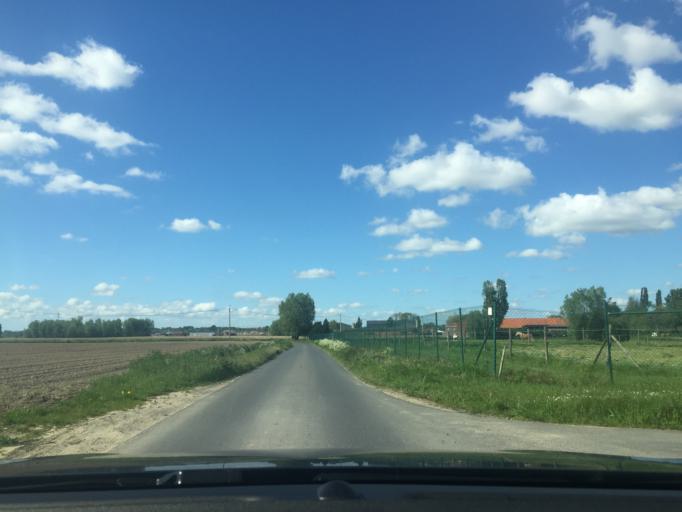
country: BE
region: Flanders
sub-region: Provincie West-Vlaanderen
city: Ardooie
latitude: 50.9847
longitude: 3.1893
